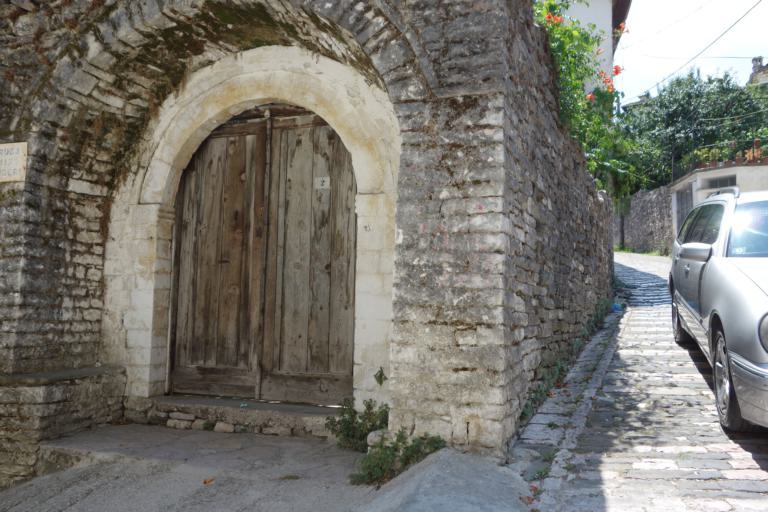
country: AL
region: Gjirokaster
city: Gjirokaster
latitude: 40.0766
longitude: 20.1400
